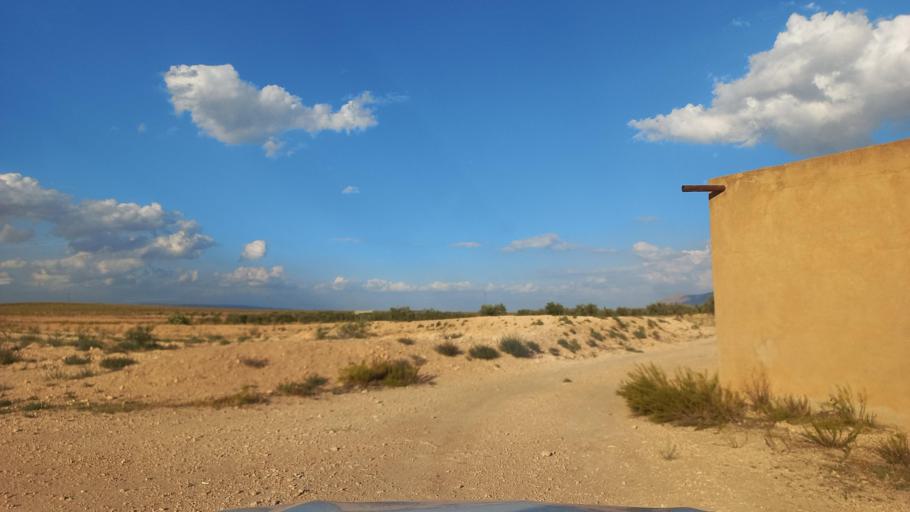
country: TN
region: Al Qasrayn
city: Sbiba
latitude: 35.3916
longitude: 9.0551
